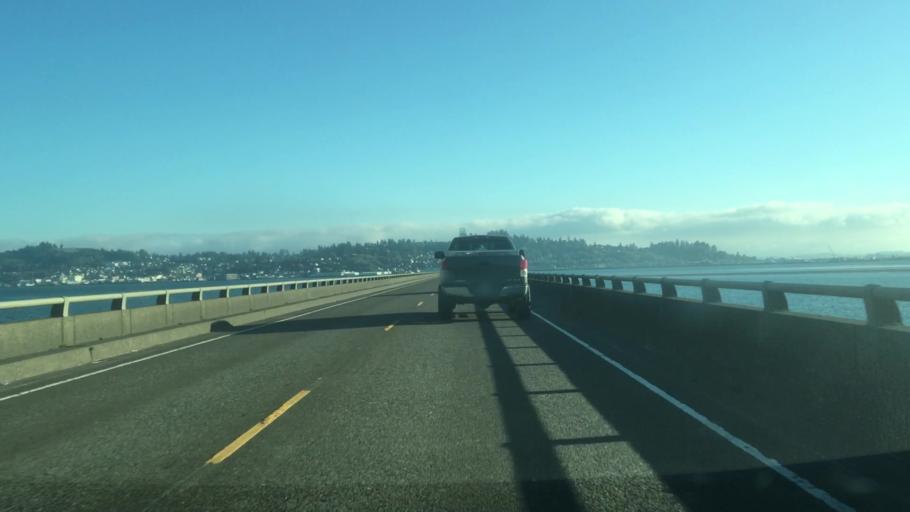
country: US
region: Oregon
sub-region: Clatsop County
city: Astoria
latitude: 46.2134
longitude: -123.8609
